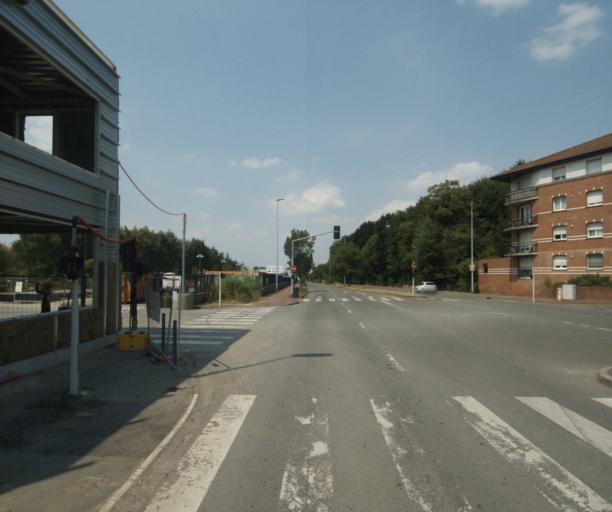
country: FR
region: Nord-Pas-de-Calais
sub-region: Departement du Nord
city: Mouvaux
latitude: 50.7190
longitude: 3.1394
